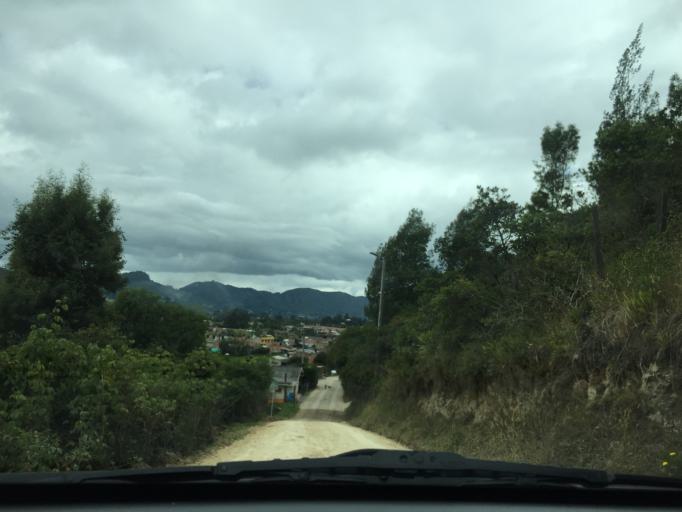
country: CO
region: Cundinamarca
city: Tabio
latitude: 4.9192
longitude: -74.1060
